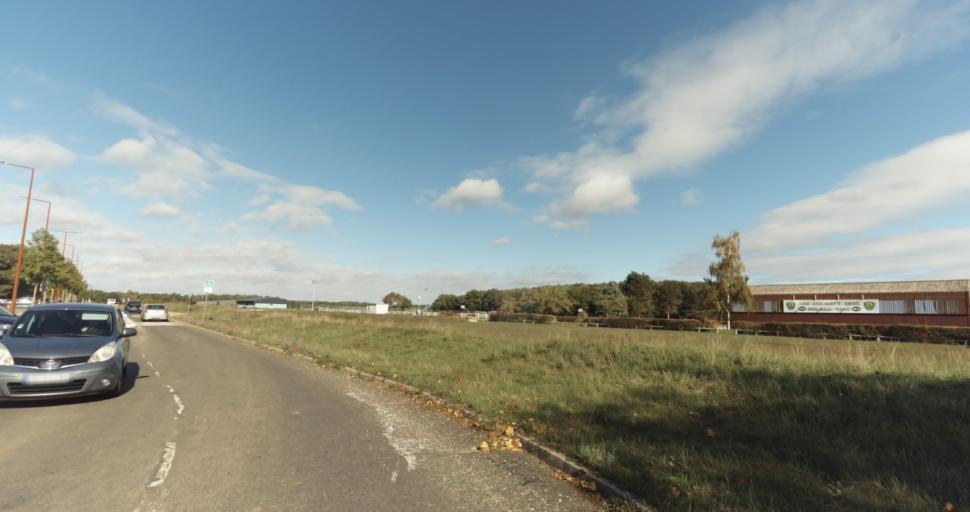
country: FR
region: Centre
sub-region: Departement d'Eure-et-Loir
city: Garnay
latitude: 48.7338
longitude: 1.3319
